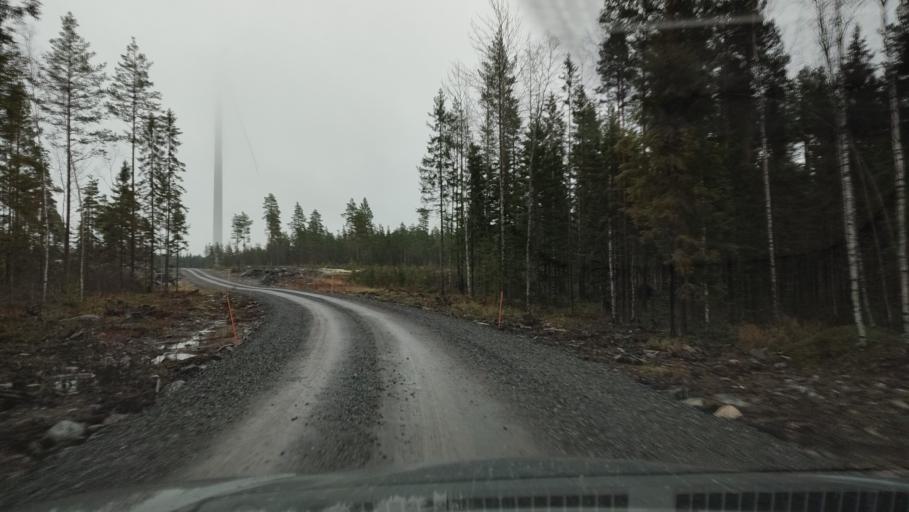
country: FI
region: Southern Ostrobothnia
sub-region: Suupohja
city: Karijoki
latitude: 62.1596
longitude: 21.5909
